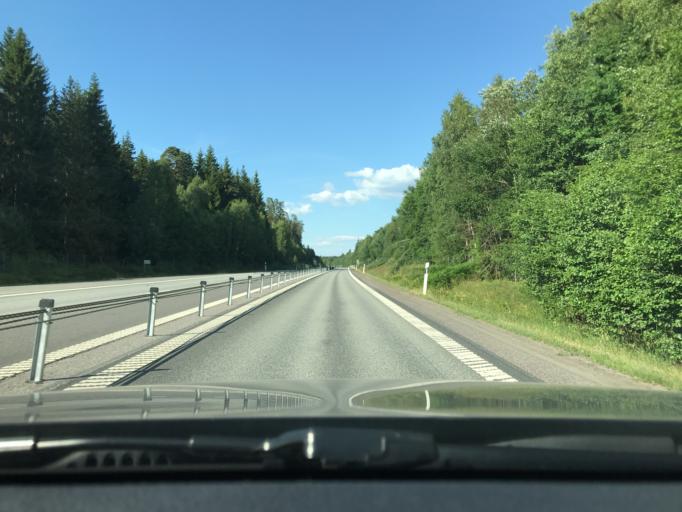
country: SE
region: Skane
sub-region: Osby Kommun
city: Osby
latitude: 56.4062
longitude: 14.0421
